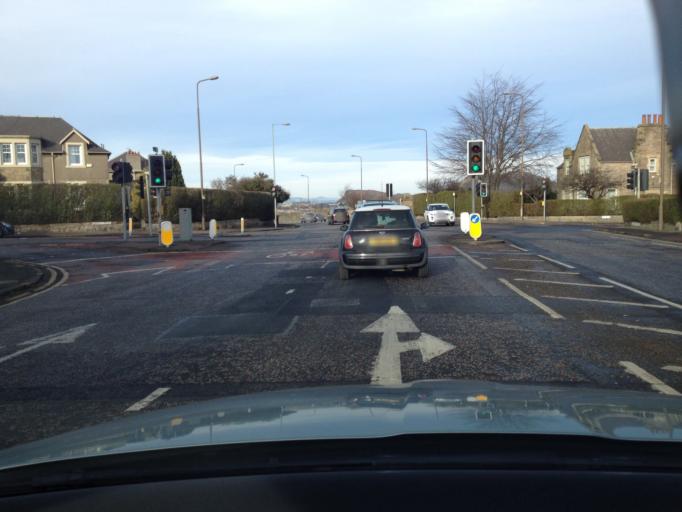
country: GB
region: Scotland
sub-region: Midlothian
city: Loanhead
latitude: 55.9122
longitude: -3.1633
